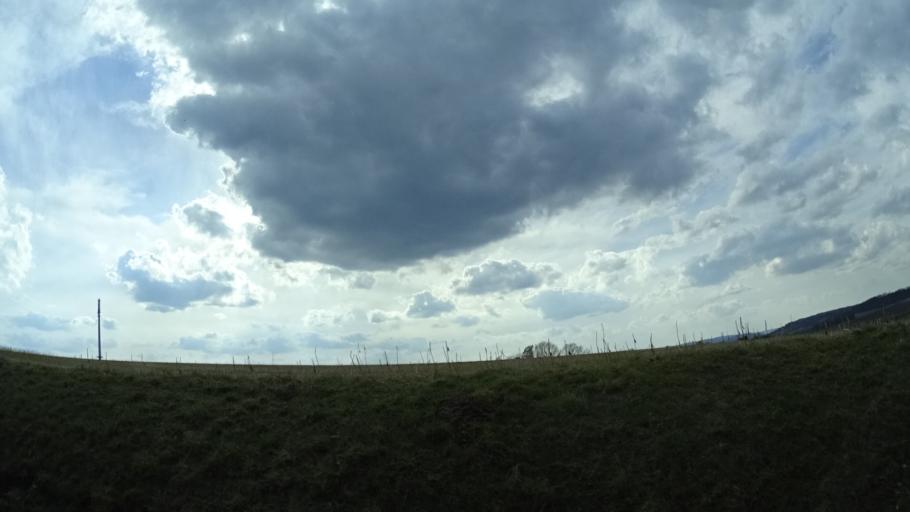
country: DE
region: Thuringia
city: Serba
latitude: 50.9455
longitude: 11.8248
